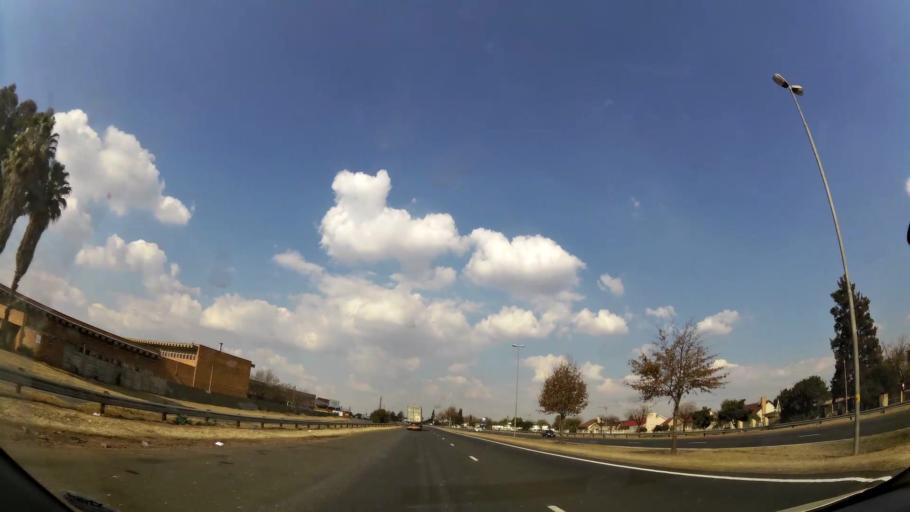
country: ZA
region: Gauteng
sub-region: Ekurhuleni Metropolitan Municipality
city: Germiston
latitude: -26.2989
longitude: 28.1797
